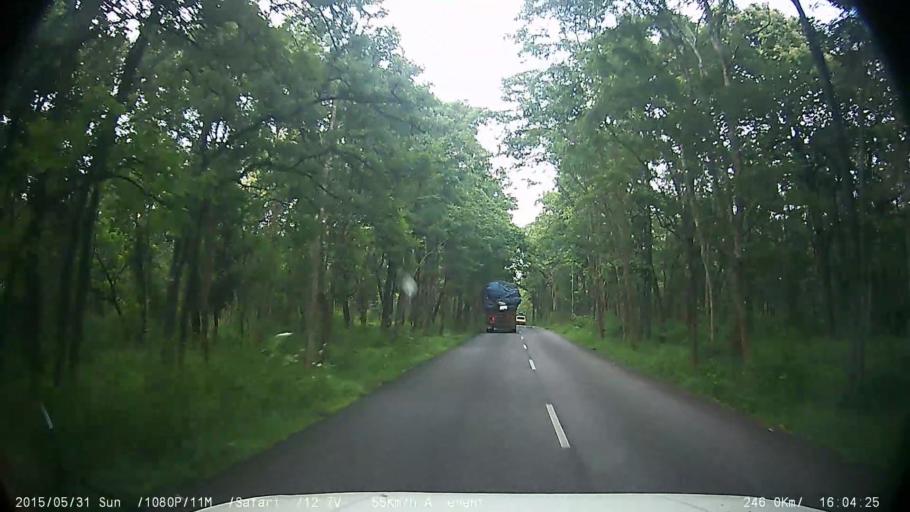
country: IN
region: Tamil Nadu
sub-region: Nilgiri
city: Naduvattam
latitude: 11.7098
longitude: 76.4157
